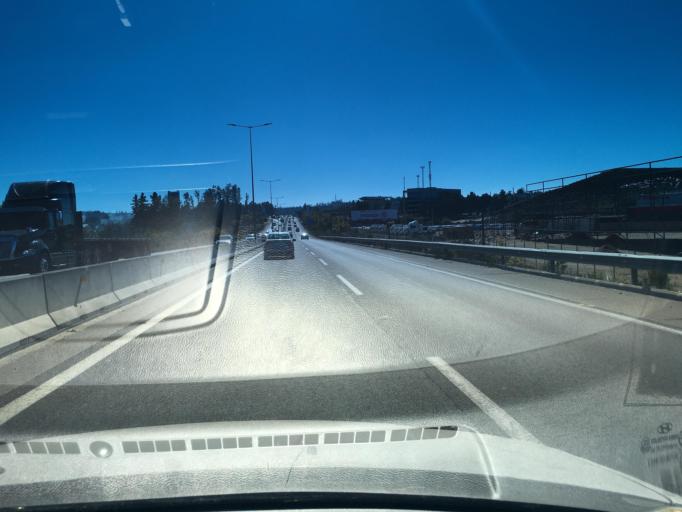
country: CL
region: Valparaiso
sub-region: Provincia de Valparaiso
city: Vina del Mar
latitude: -33.1371
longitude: -71.5628
